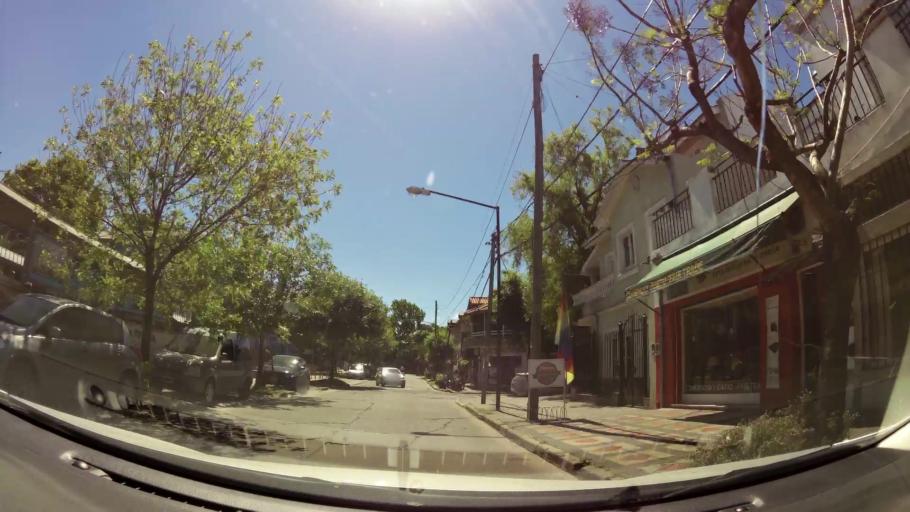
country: AR
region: Buenos Aires
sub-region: Partido de San Isidro
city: San Isidro
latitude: -34.4654
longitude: -58.5079
